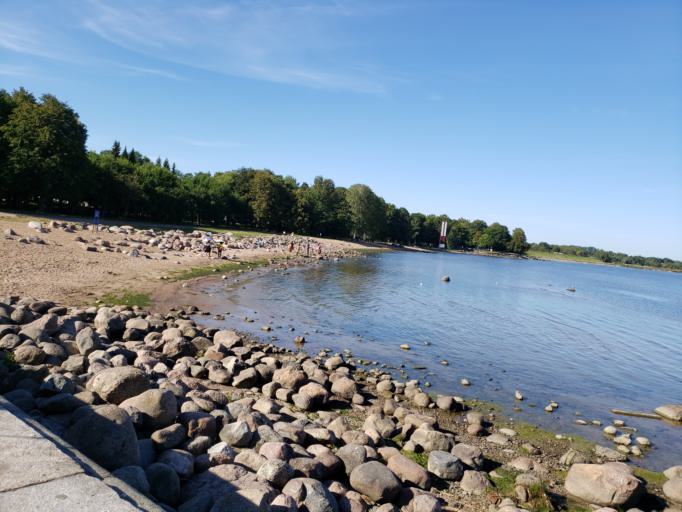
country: RU
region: St.-Petersburg
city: Peterhof
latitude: 59.8896
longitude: 29.9112
